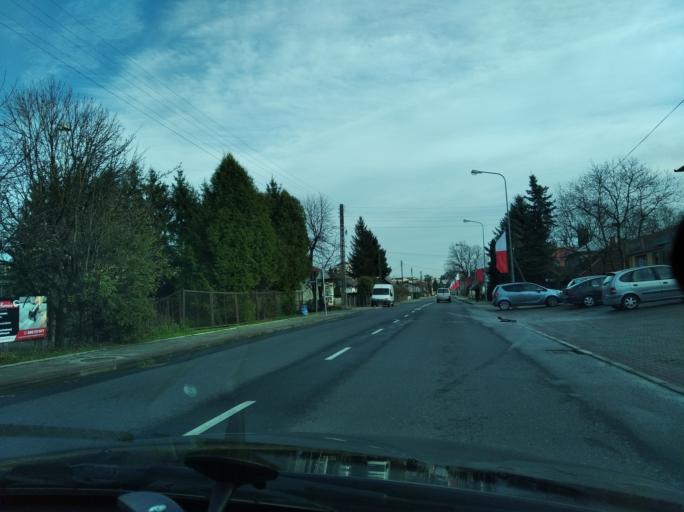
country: PL
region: Subcarpathian Voivodeship
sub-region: Powiat ropczycko-sedziszowski
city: Sedziszow Malopolski
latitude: 50.0692
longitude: 21.6912
